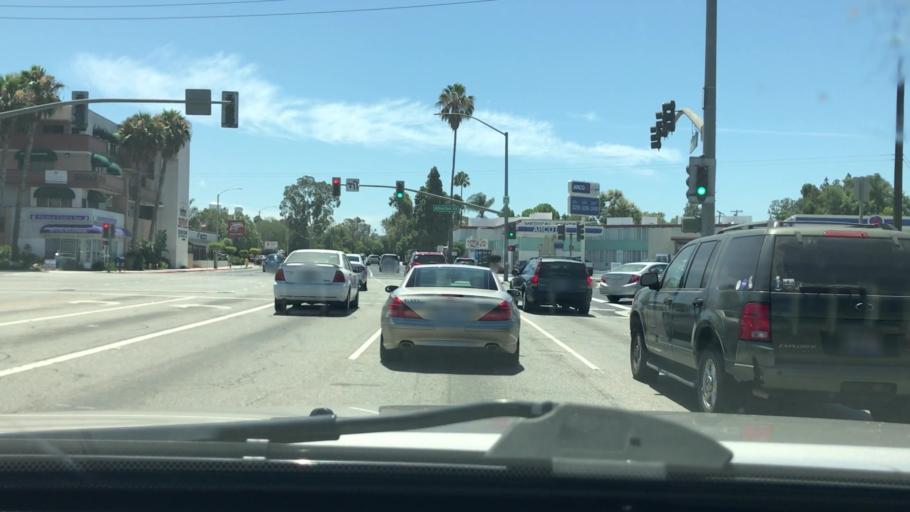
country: US
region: California
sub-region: Orange County
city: Rossmoor
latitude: 33.7888
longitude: -118.1247
